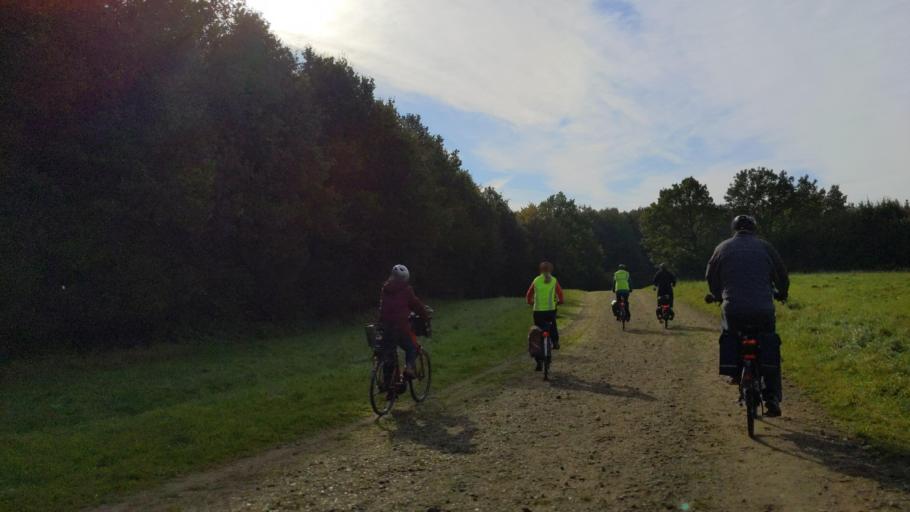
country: DE
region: Schleswig-Holstein
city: Badendorf
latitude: 53.8760
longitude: 10.5859
